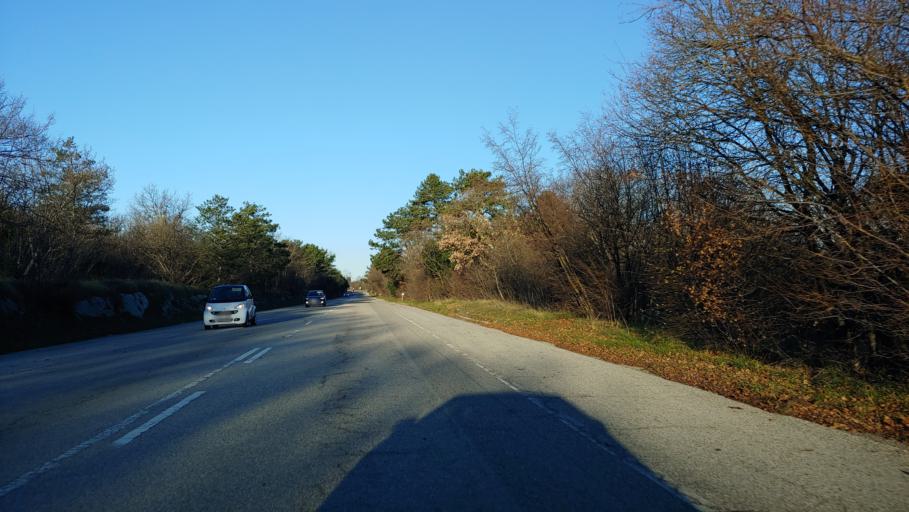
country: IT
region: Friuli Venezia Giulia
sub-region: Provincia di Trieste
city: Villa Opicina
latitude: 45.6757
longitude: 13.8142
